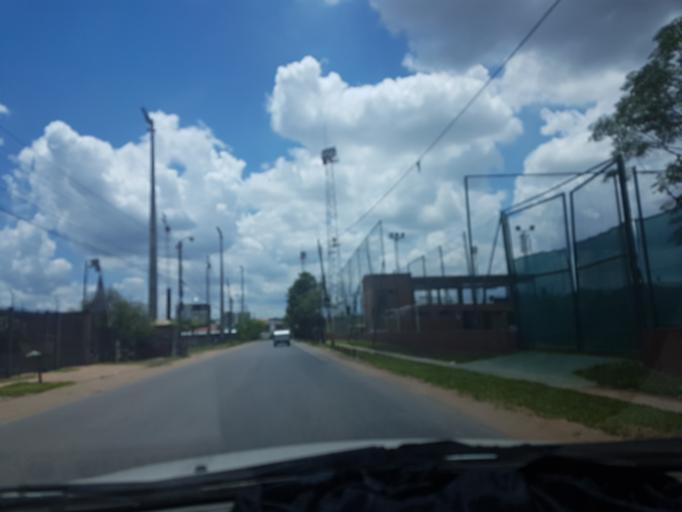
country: PY
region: Central
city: Fernando de la Mora
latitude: -25.2863
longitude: -57.5445
